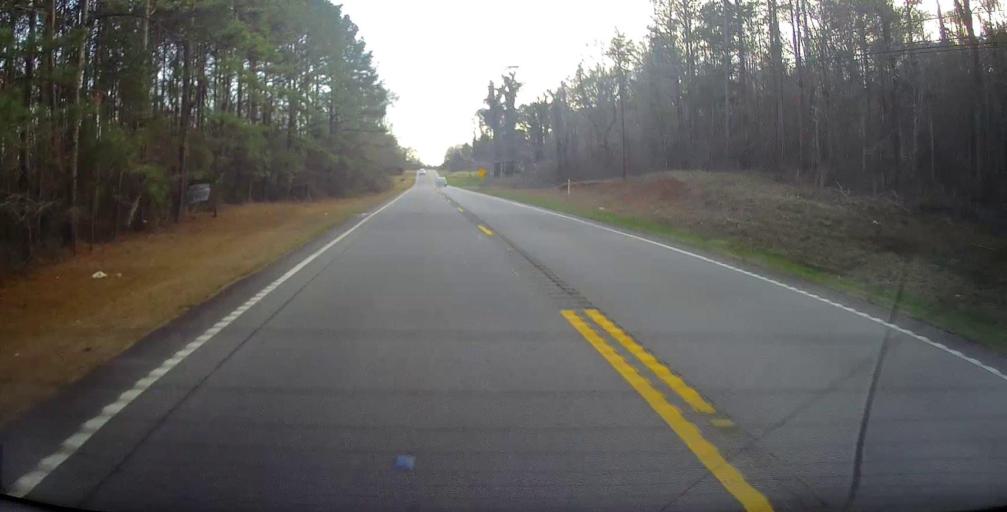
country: US
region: Georgia
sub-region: Troup County
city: West Point
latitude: 32.9069
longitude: -85.1583
